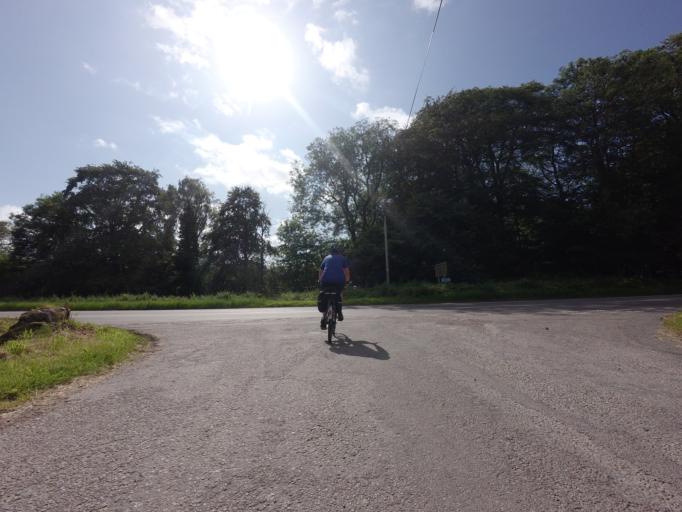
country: GB
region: Scotland
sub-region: Highland
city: Nairn
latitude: 57.5533
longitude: -3.8651
